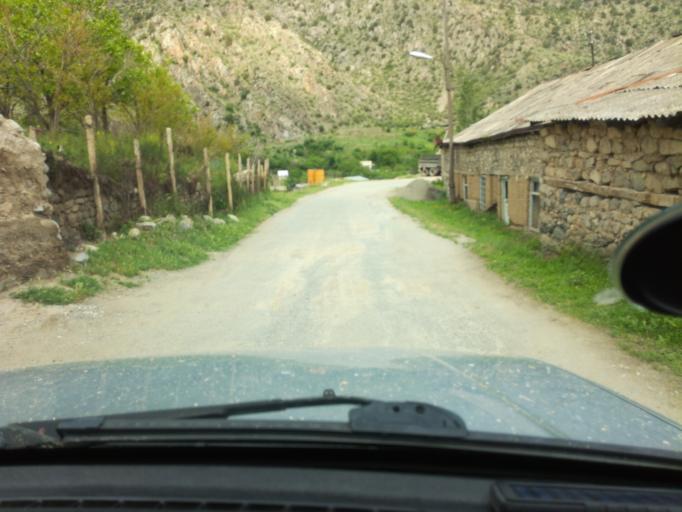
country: AM
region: Syunik'i Marz
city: Meghri
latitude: 38.9396
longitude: 46.2158
